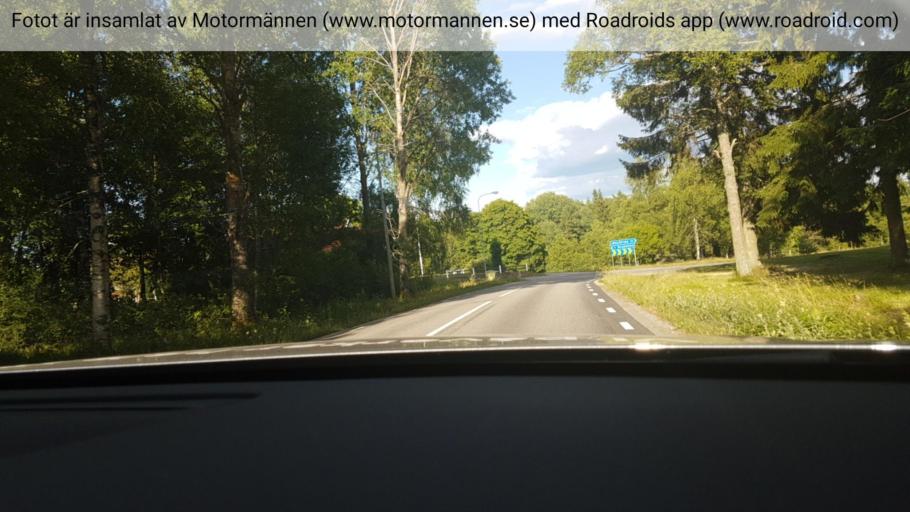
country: SE
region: Vaestra Goetaland
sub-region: Tranemo Kommun
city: Limmared
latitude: 57.5693
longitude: 13.5718
